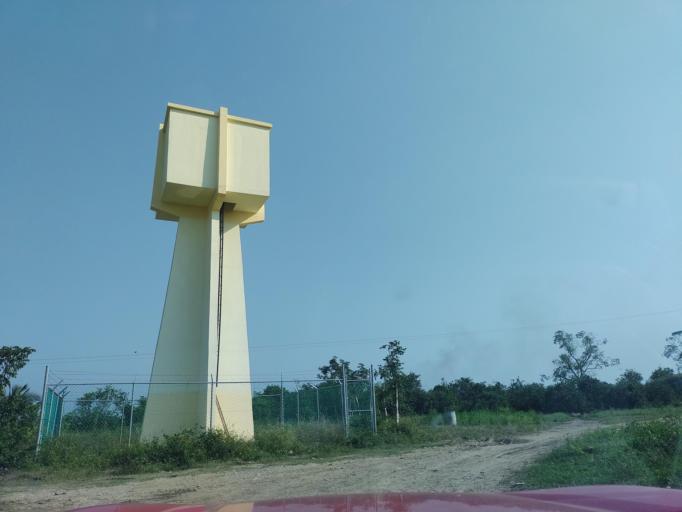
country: MX
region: Veracruz
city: Agua Dulce
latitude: 20.3673
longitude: -97.1850
